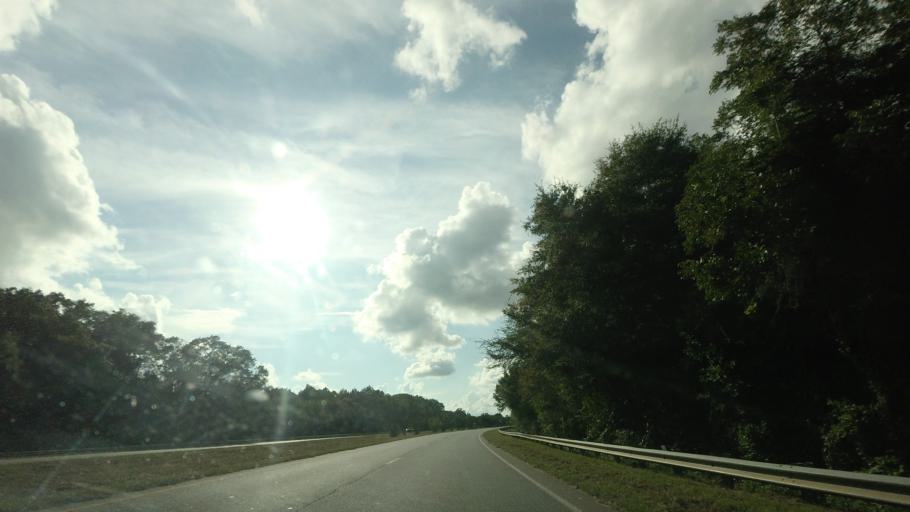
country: US
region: Georgia
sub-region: Pulaski County
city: Hawkinsville
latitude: 32.2818
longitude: -83.4563
